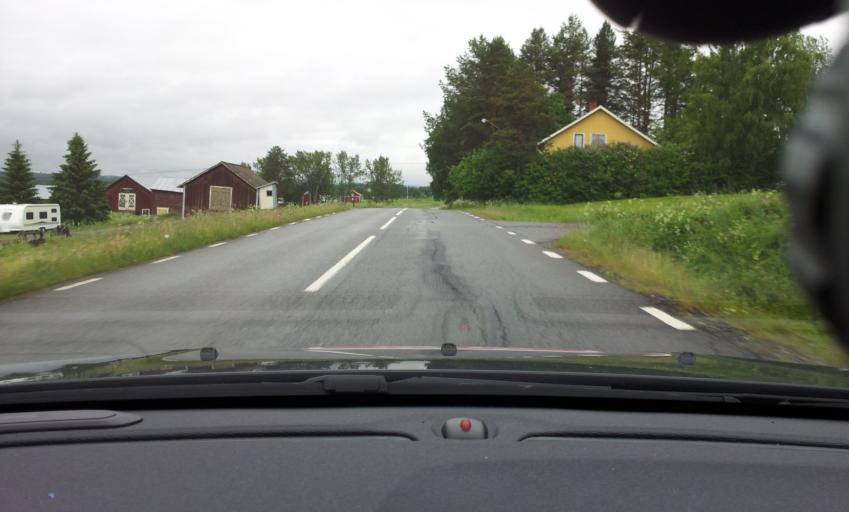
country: SE
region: Jaemtland
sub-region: Stroemsunds Kommun
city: Stroemsund
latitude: 63.5614
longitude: 15.3979
